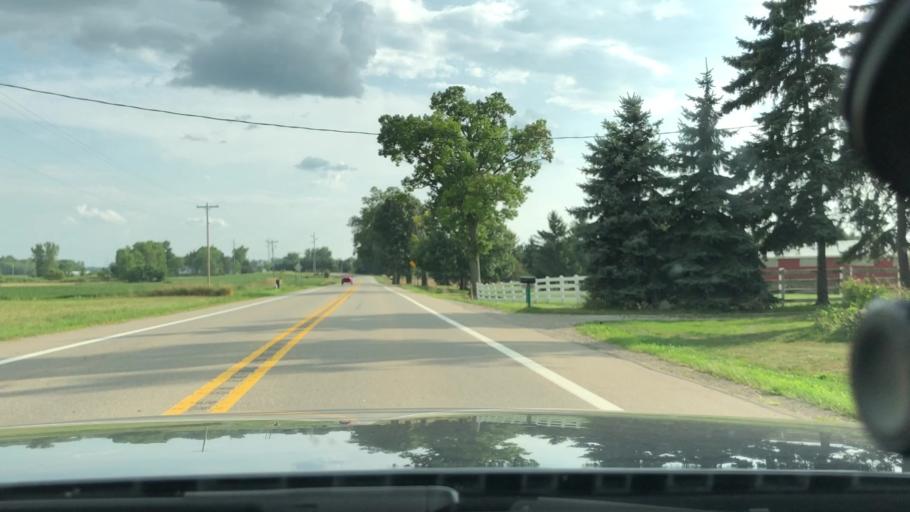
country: US
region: Michigan
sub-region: Washtenaw County
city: Chelsea
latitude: 42.2756
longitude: -84.0322
